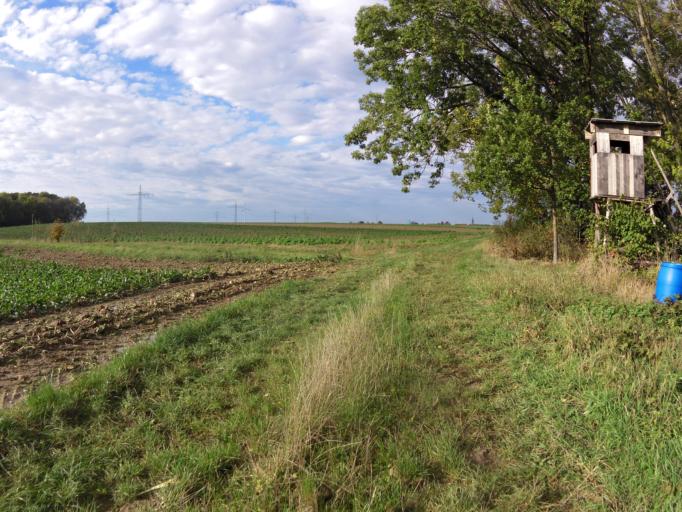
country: DE
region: Bavaria
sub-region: Regierungsbezirk Unterfranken
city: Biebelried
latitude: 49.7317
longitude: 10.0697
